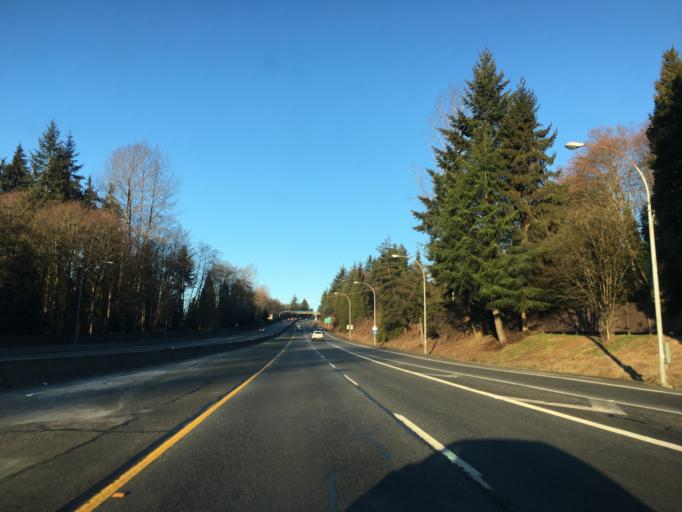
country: CA
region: British Columbia
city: West Vancouver
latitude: 49.3380
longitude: -123.1384
